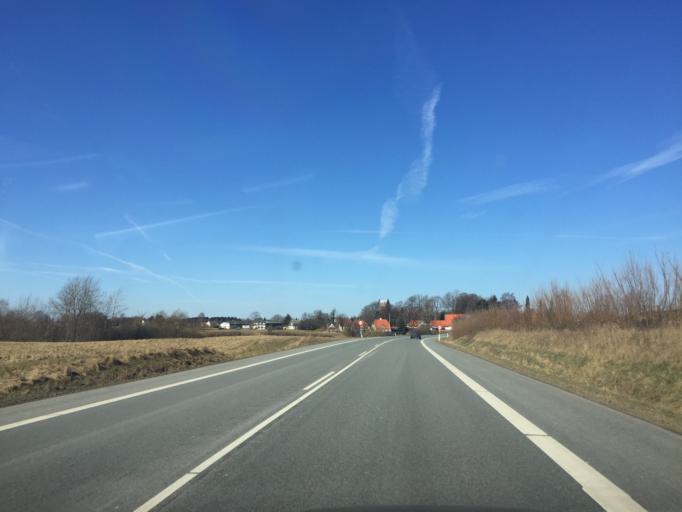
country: DK
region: Capital Region
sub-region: Fredensborg Kommune
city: Fredensborg
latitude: 56.0145
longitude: 12.4584
